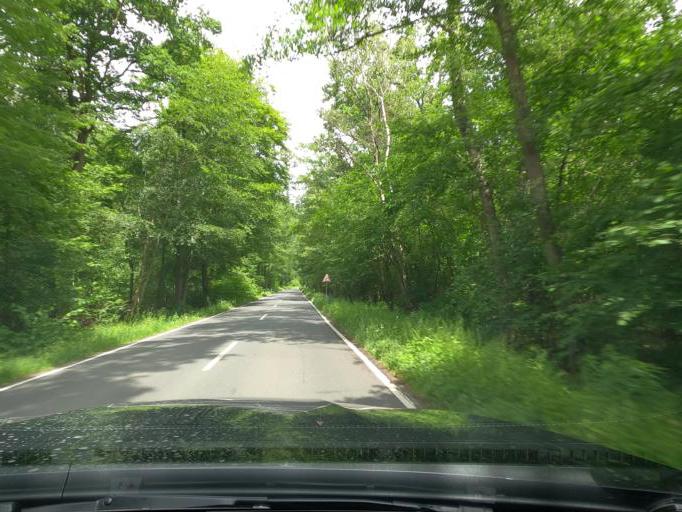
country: DE
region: Lower Saxony
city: Lehrte
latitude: 52.4015
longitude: 9.9280
